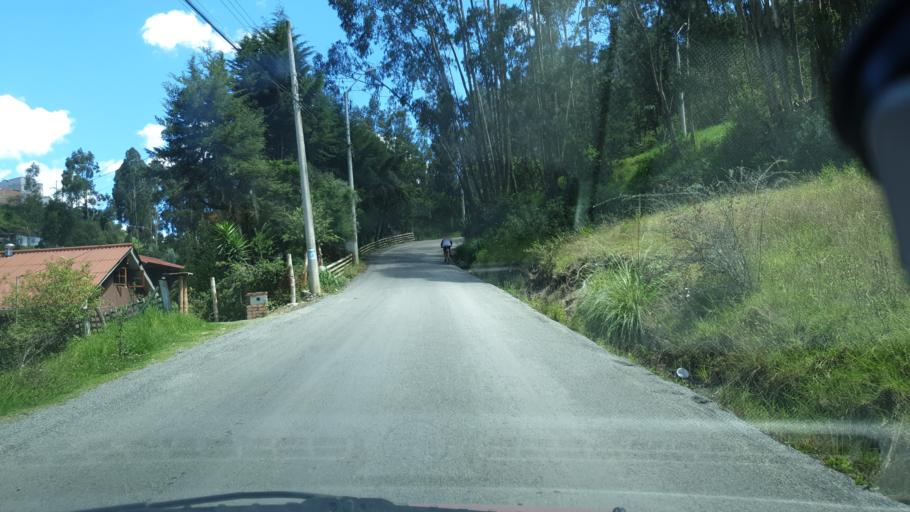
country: EC
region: Azuay
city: Cuenca
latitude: -2.8766
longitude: -78.9514
